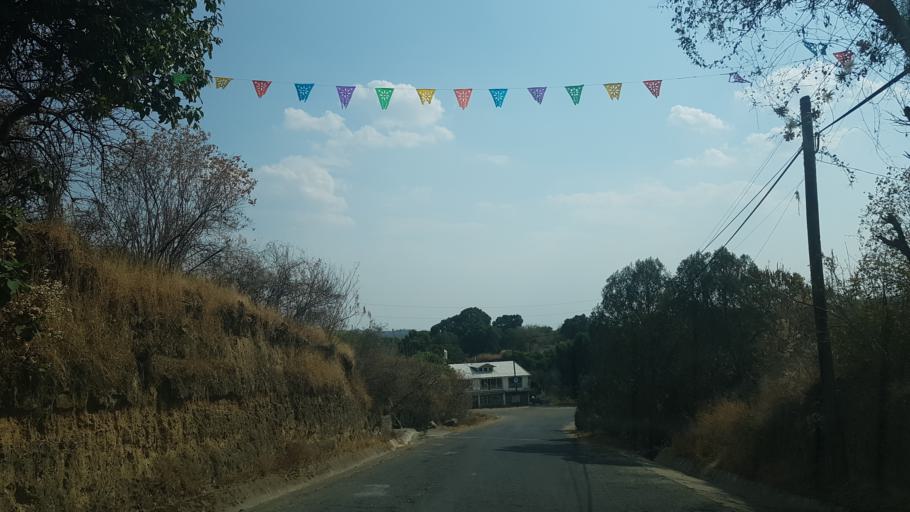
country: MX
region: Puebla
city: San Juan Amecac
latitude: 18.8308
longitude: -98.7048
